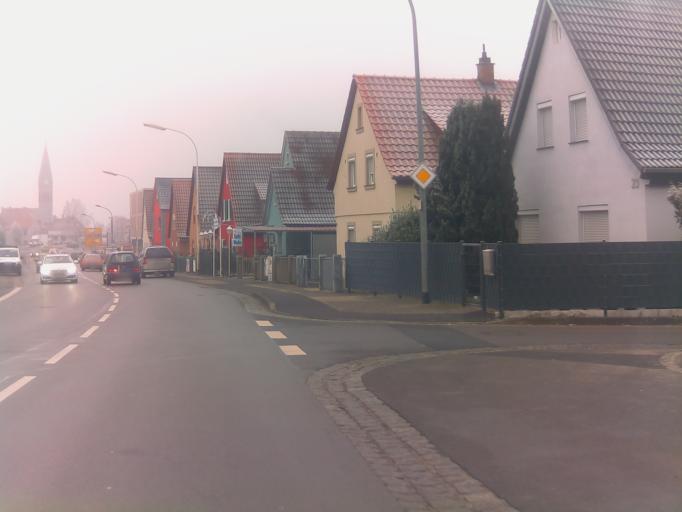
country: DE
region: Bavaria
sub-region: Regierungsbezirk Unterfranken
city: Hassfurt
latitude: 50.0354
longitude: 10.5145
